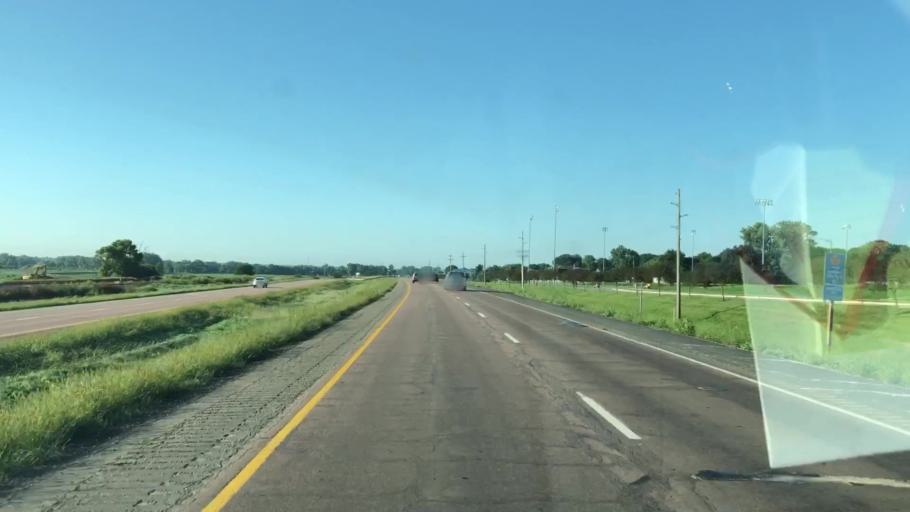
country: US
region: Iowa
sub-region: Woodbury County
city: Sioux City
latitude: 42.6213
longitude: -96.2937
